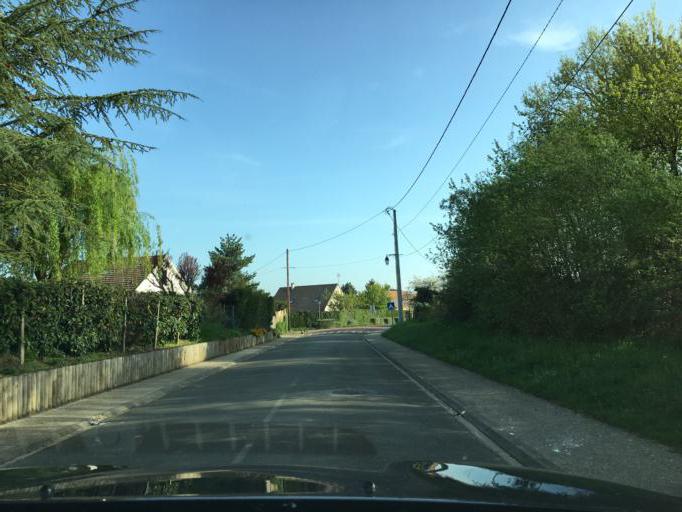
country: FR
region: Ile-de-France
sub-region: Departement des Yvelines
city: Conde-sur-Vesgre
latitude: 48.7259
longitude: 1.6559
